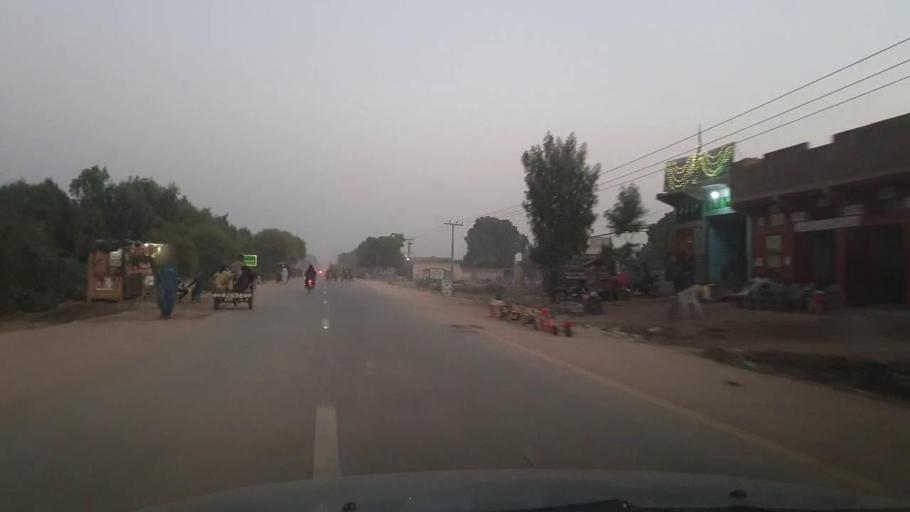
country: PK
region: Sindh
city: Tando Allahyar
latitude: 25.4502
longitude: 68.7266
